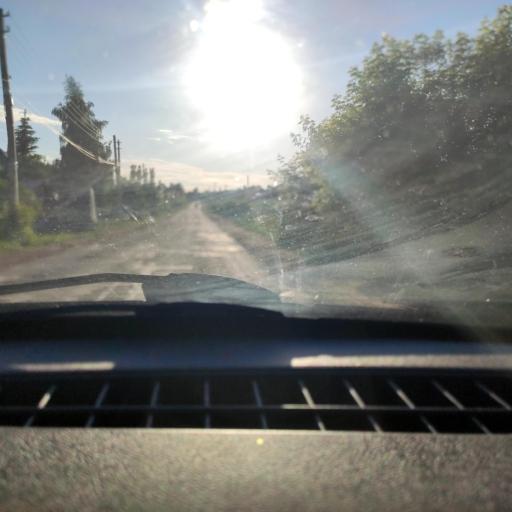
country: RU
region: Bashkortostan
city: Avdon
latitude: 54.6203
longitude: 55.6624
